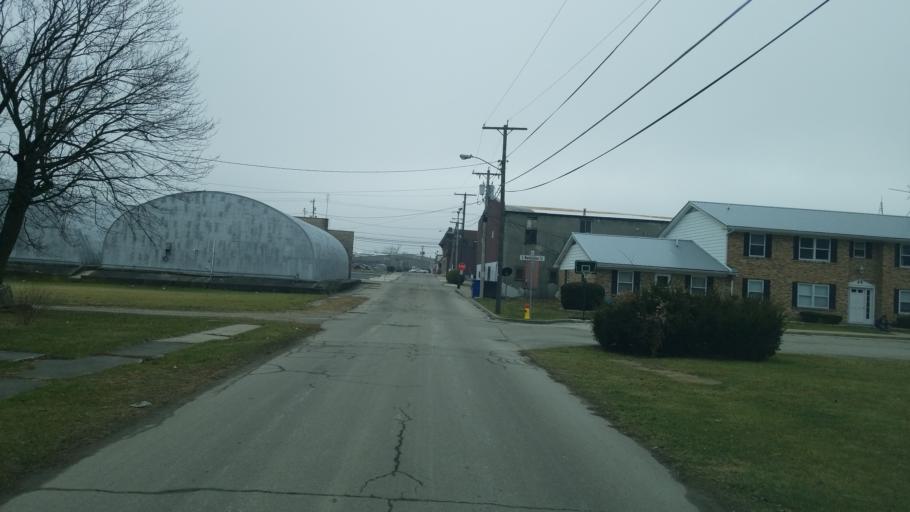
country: US
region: Indiana
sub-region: Adams County
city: Berne
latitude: 40.6596
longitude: -84.9495
